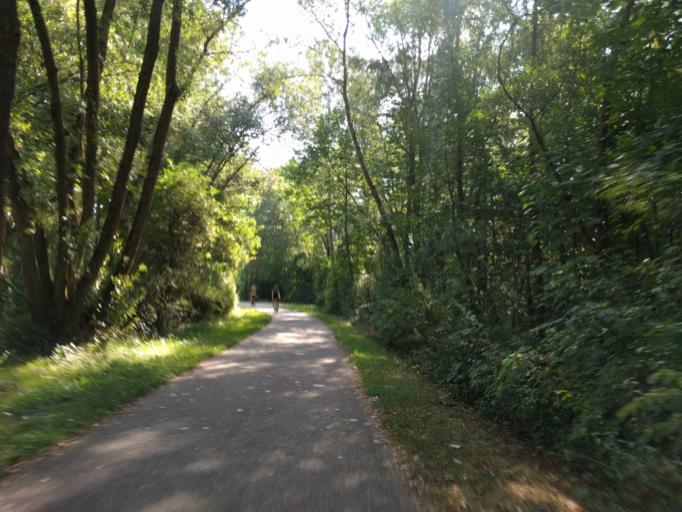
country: DE
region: Bavaria
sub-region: Upper Palatinate
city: Tegernheim
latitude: 49.0199
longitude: 12.1571
